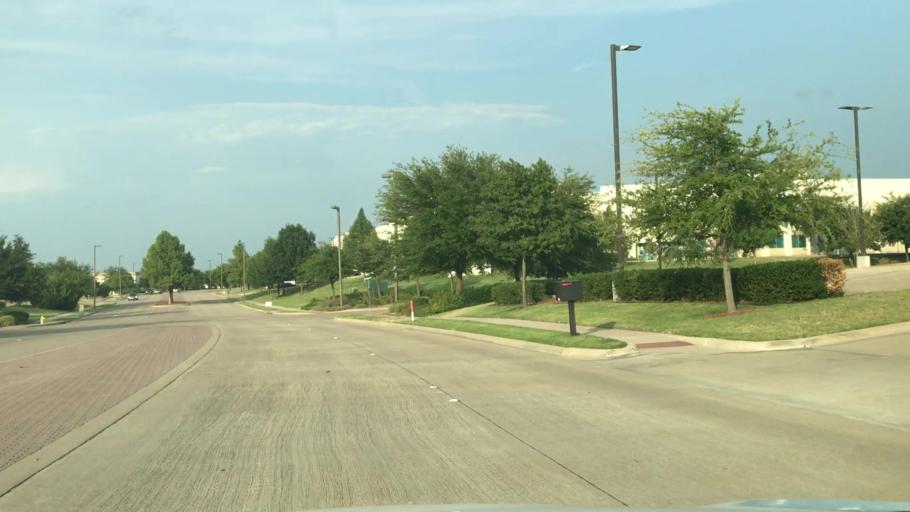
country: US
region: Texas
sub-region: Rockwall County
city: Rockwall
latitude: 32.9092
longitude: -96.4248
